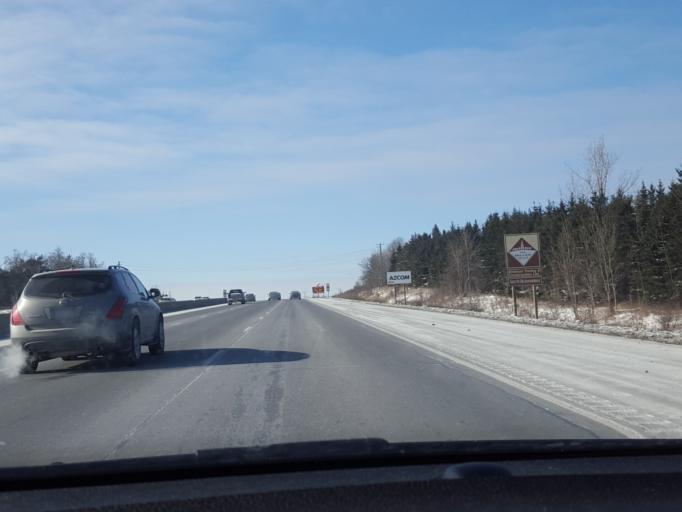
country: CA
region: Ontario
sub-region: Halton
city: Milton
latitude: 43.5179
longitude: -79.9405
